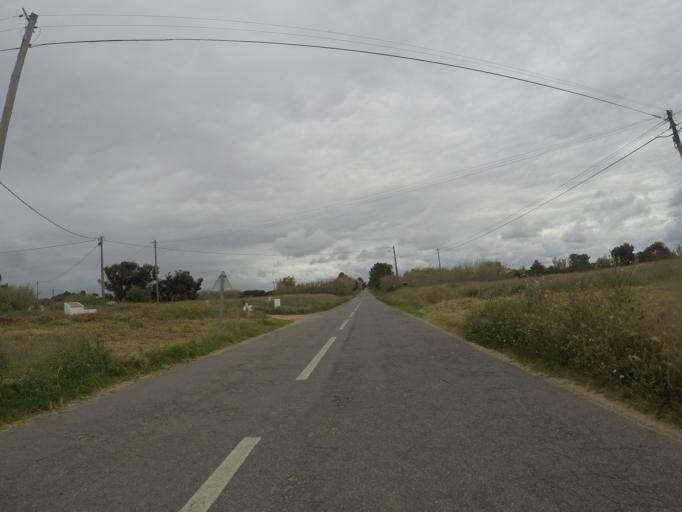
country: PT
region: Beja
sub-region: Odemira
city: Vila Nova de Milfontes
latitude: 37.6002
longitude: -8.8048
